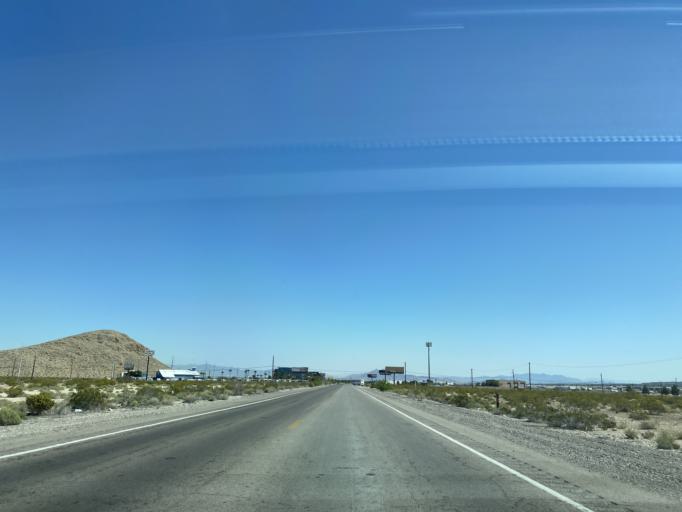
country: US
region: Nevada
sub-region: Clark County
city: Enterprise
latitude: 35.9454
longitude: -115.1799
